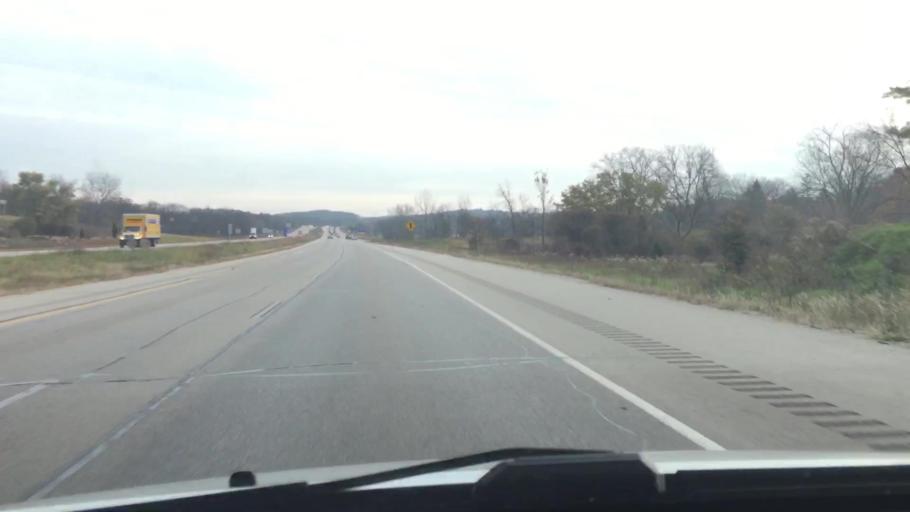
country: US
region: Wisconsin
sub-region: Waukesha County
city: Muskego
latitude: 42.9332
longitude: -88.1586
